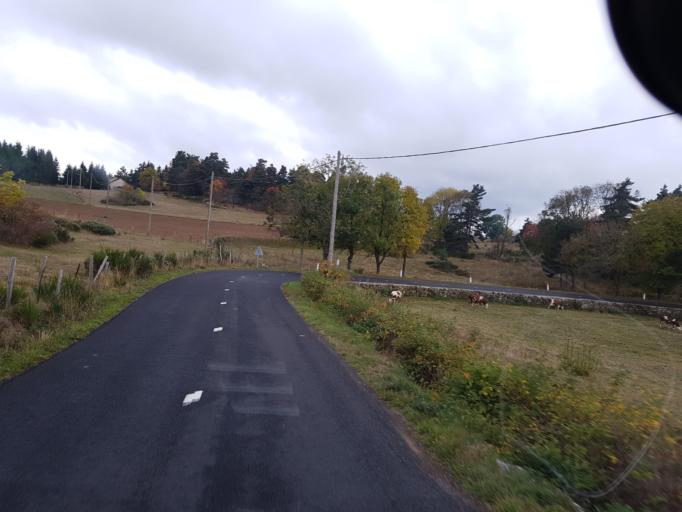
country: FR
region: Languedoc-Roussillon
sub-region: Departement de la Lozere
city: Langogne
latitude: 44.7208
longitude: 3.7805
